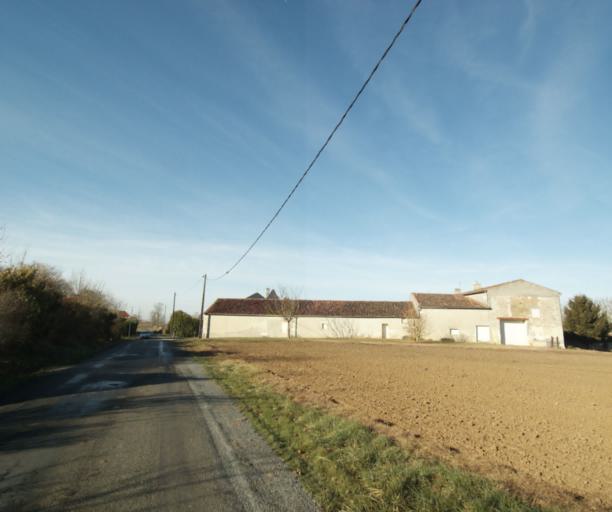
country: FR
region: Poitou-Charentes
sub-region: Departement de la Charente-Maritime
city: Chaniers
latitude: 45.7382
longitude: -0.5618
